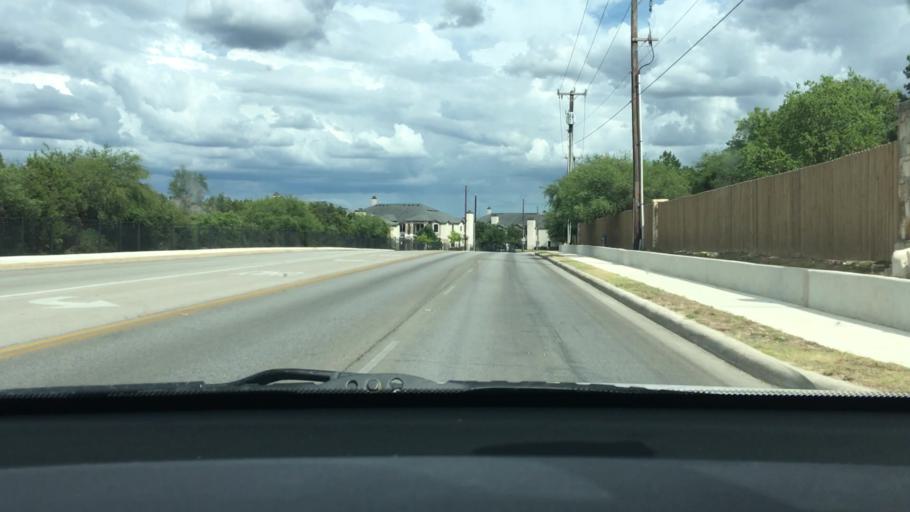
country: US
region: Texas
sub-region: Bexar County
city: Timberwood Park
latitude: 29.6541
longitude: -98.4285
